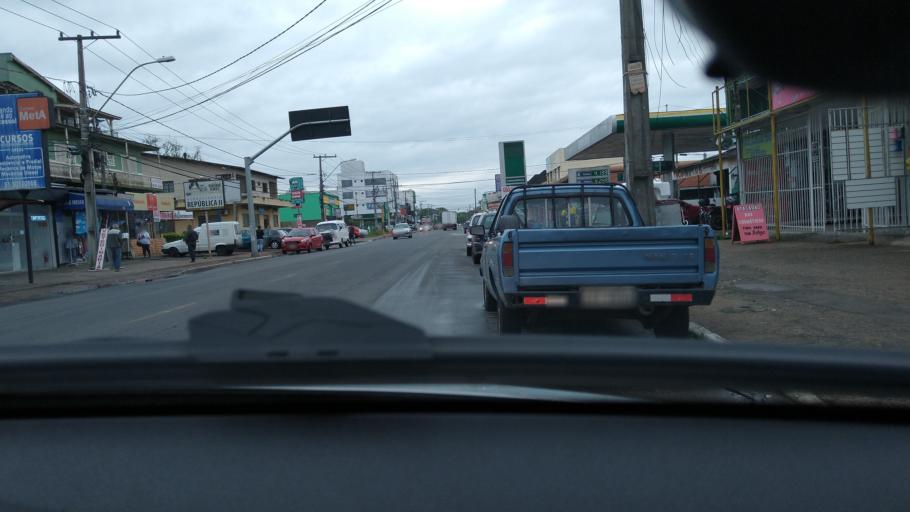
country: BR
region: Rio Grande do Sul
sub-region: Canoas
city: Canoas
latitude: -29.9025
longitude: -51.1966
